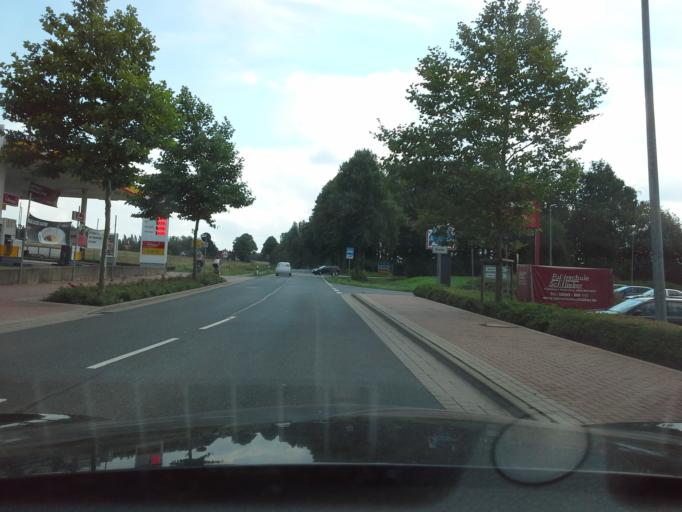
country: DE
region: Lower Saxony
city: Lauenau
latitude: 52.2678
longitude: 9.3702
